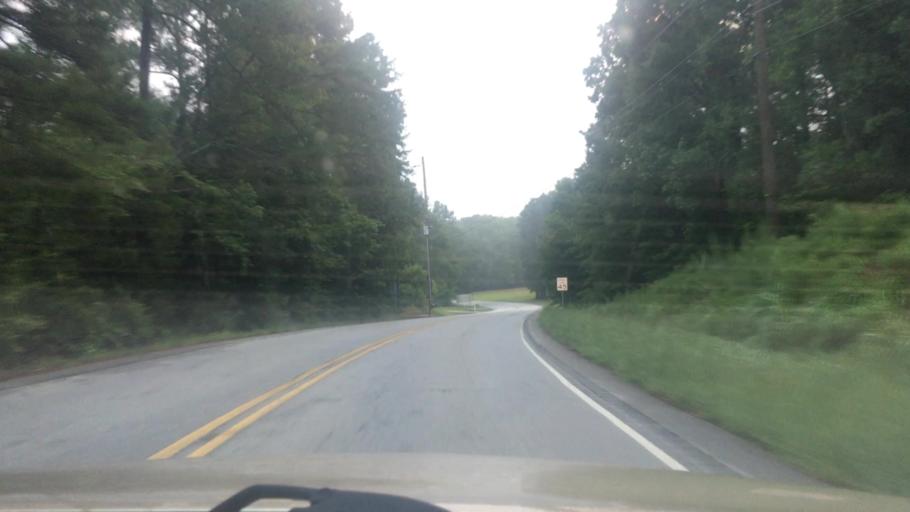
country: US
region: South Carolina
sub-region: Lexington County
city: Irmo
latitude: 34.1313
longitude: -81.1775
